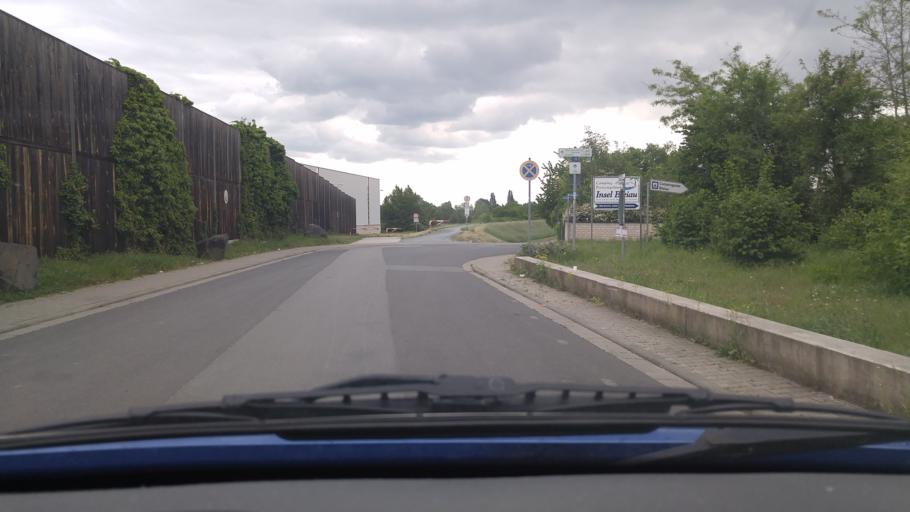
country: DE
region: Hesse
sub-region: Regierungsbezirk Darmstadt
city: Ginsheim-Gustavsburg
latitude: 49.9877
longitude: 8.3157
